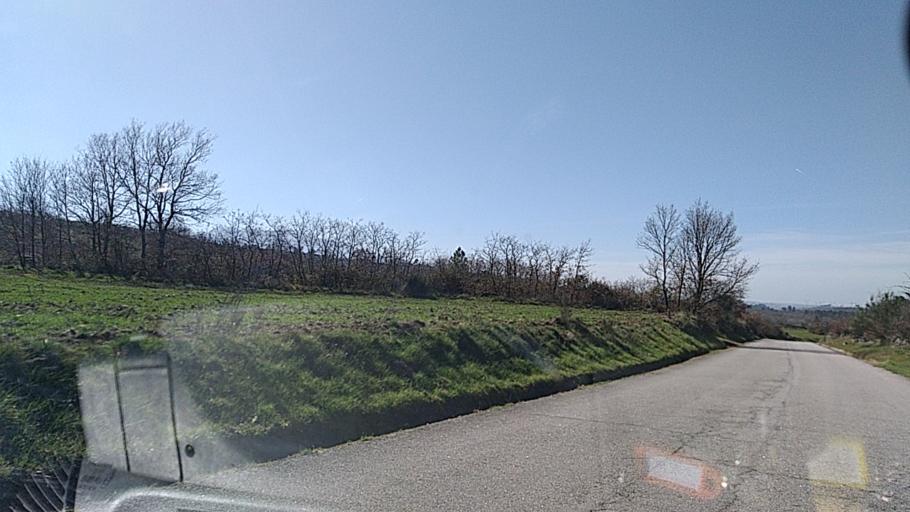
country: PT
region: Guarda
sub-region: Fornos de Algodres
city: Fornos de Algodres
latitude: 40.5900
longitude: -7.4785
